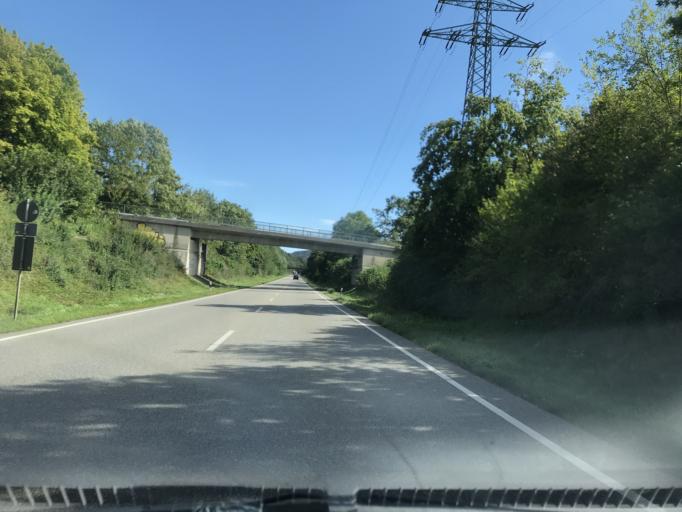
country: CH
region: Aargau
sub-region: Bezirk Rheinfelden
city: Mumpf
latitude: 47.5690
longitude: 7.9198
